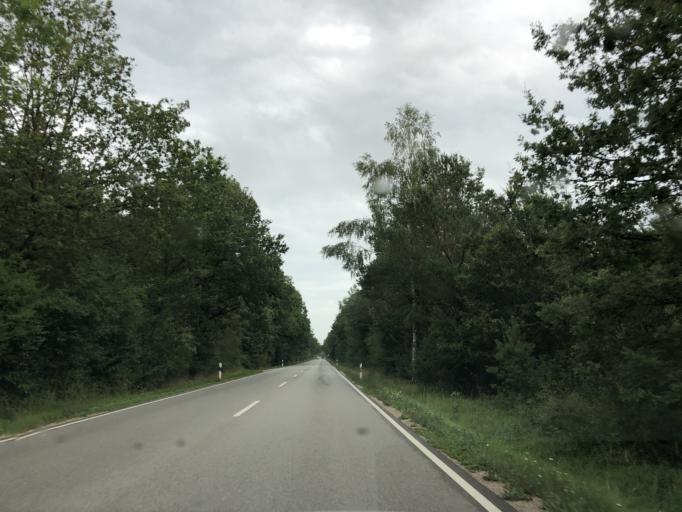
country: DE
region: Bavaria
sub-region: Upper Bavaria
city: Unterschleissheim
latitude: 48.2751
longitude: 11.6032
